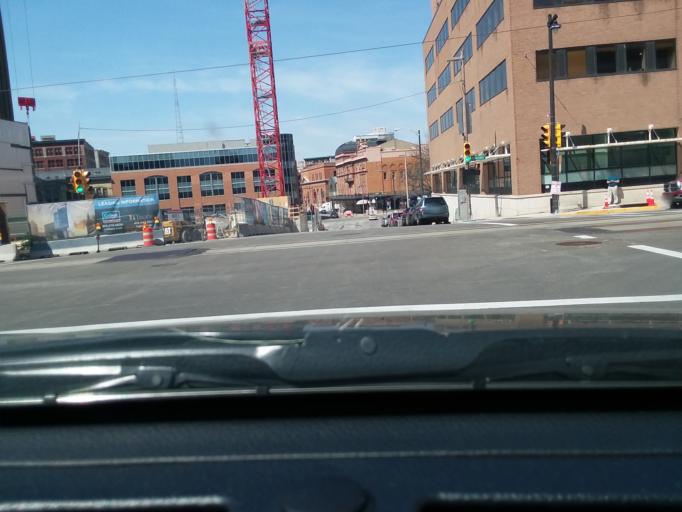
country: US
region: Wisconsin
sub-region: Milwaukee County
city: Milwaukee
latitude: 43.0412
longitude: -87.9079
